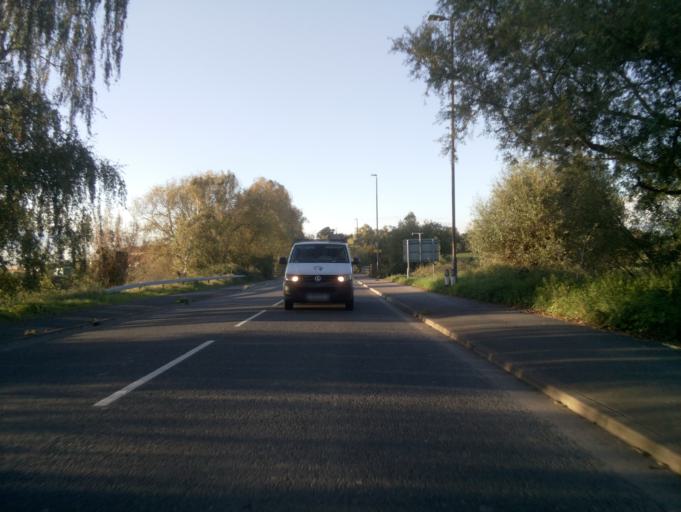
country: GB
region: England
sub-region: Gloucestershire
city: Tewkesbury
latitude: 51.9994
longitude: -2.1585
